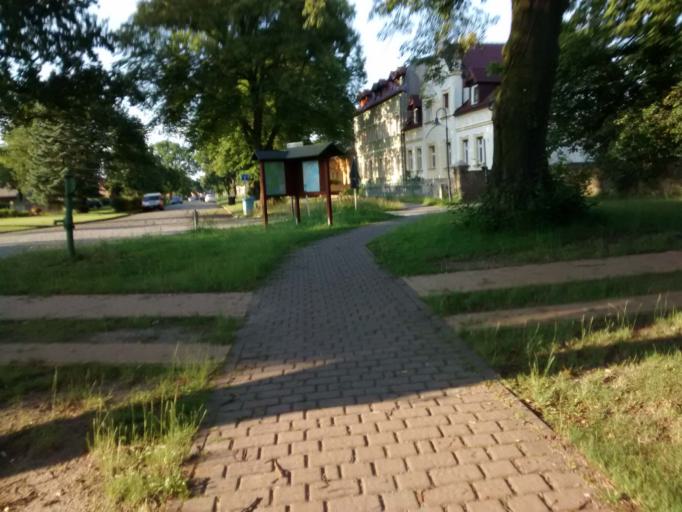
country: DE
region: Brandenburg
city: Hohen Neuendorf
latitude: 52.6606
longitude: 13.2595
